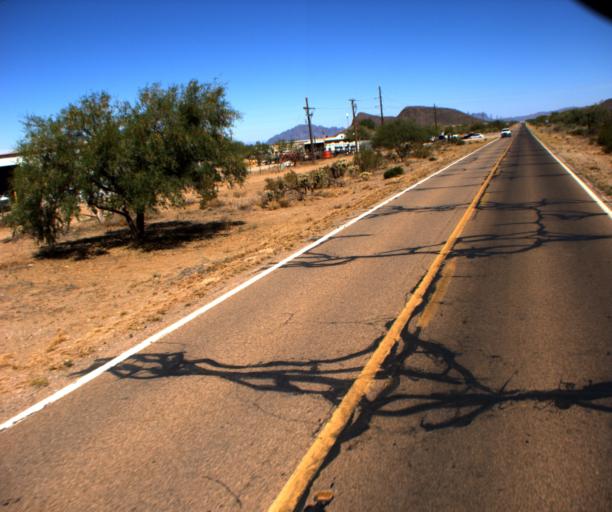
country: US
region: Arizona
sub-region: Pima County
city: Sells
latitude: 31.9346
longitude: -111.9131
